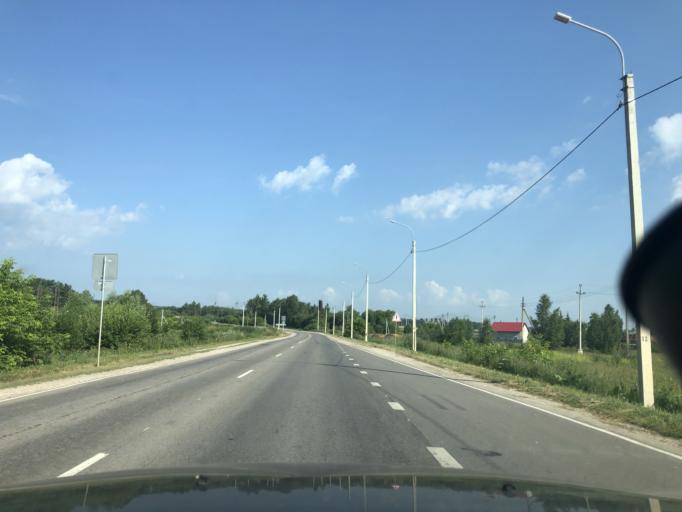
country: RU
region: Tula
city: Dubna
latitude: 54.1072
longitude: 37.1068
